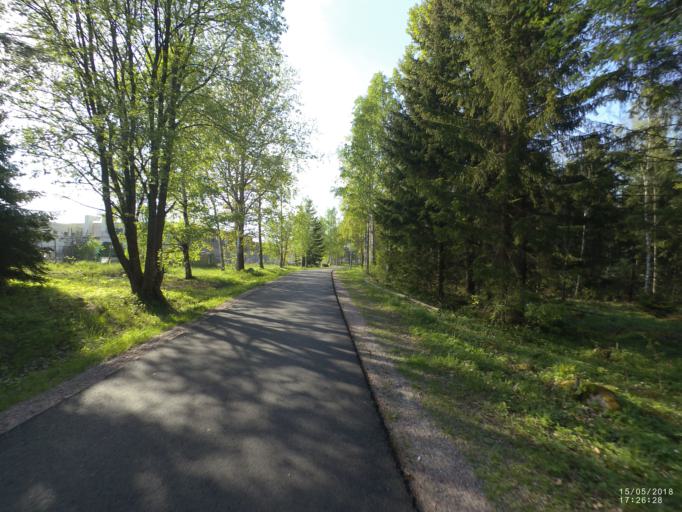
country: SE
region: Soedermanland
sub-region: Nykopings Kommun
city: Nykoping
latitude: 58.7216
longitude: 17.0260
